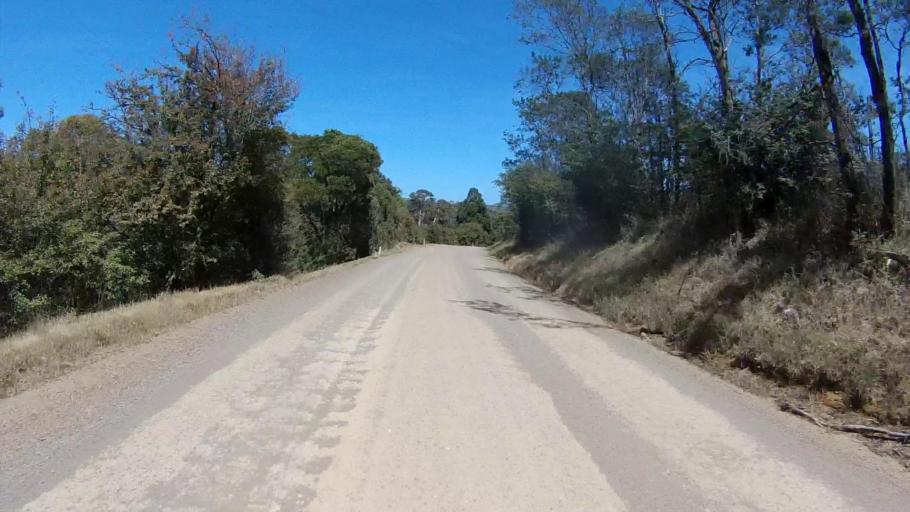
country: AU
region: Tasmania
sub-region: Sorell
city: Sorell
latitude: -42.7566
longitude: 147.6628
